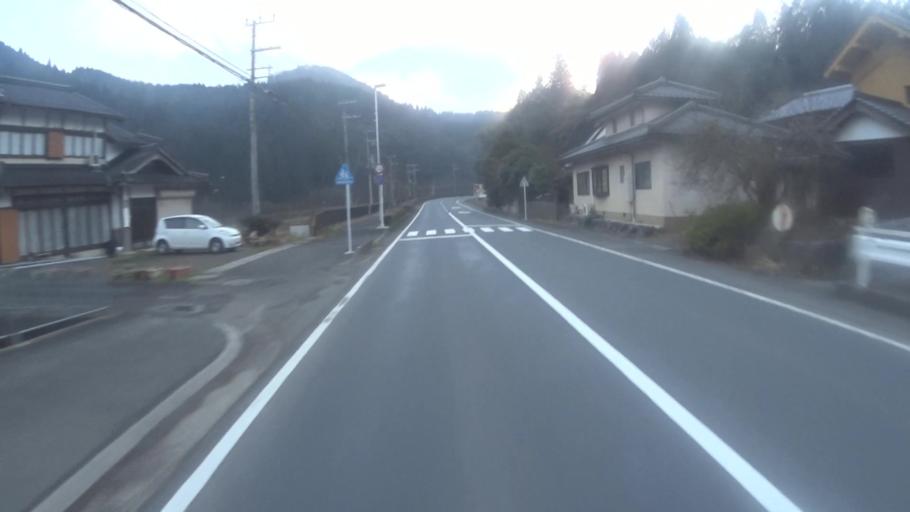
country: JP
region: Kyoto
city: Ayabe
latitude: 35.3262
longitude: 135.3317
